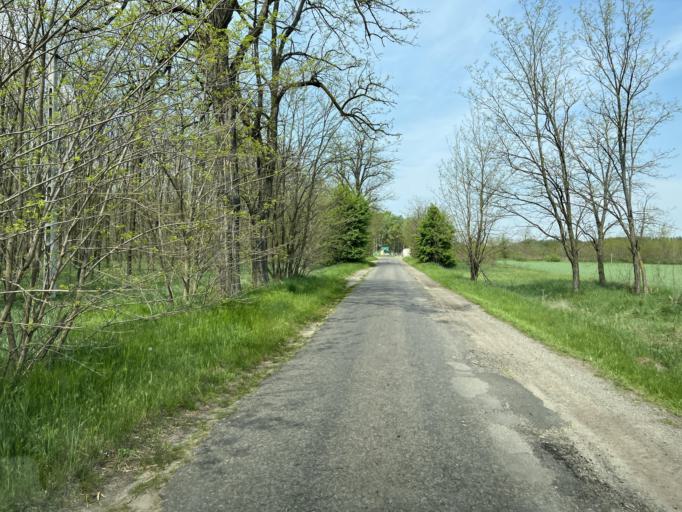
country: HU
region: Pest
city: Nagykoros
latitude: 47.0543
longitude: 19.8518
